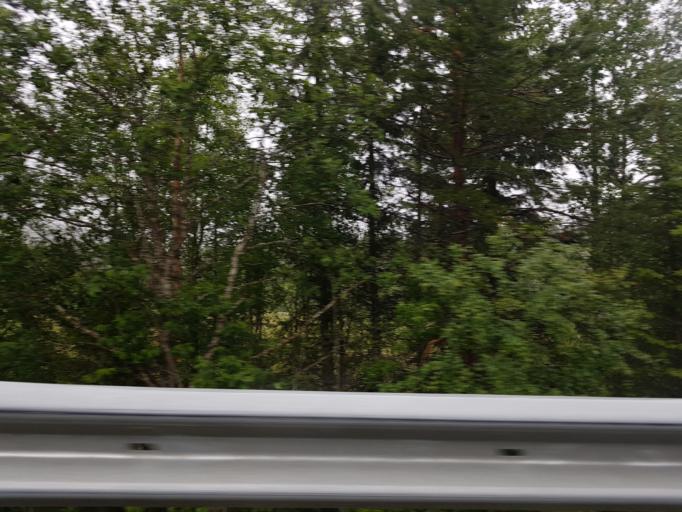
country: NO
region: Sor-Trondelag
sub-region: Selbu
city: Mebonden
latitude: 63.3408
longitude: 11.0787
